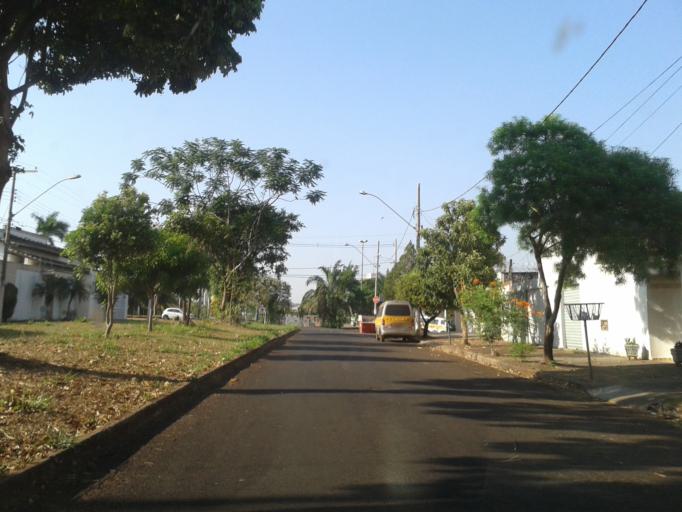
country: BR
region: Minas Gerais
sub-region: Ituiutaba
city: Ituiutaba
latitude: -18.9644
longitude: -49.4688
